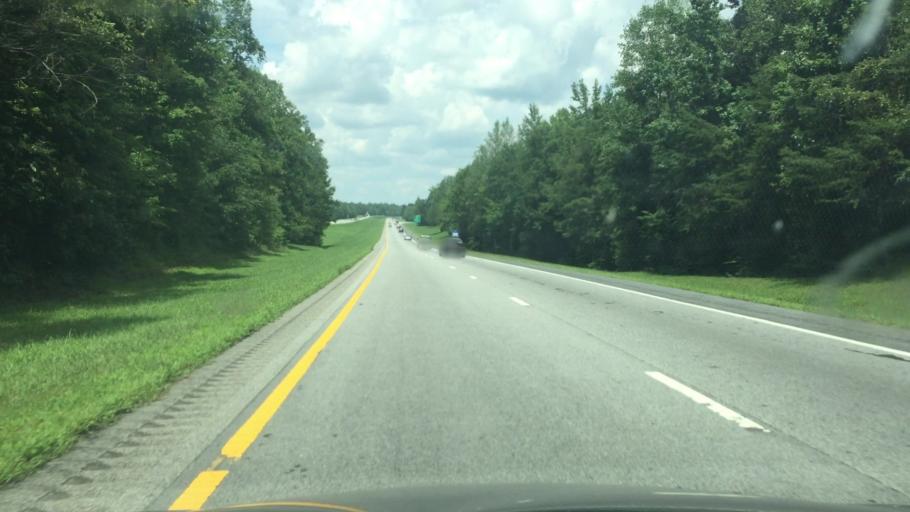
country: US
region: North Carolina
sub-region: Guilford County
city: Pleasant Garden
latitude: 35.9118
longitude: -79.8220
